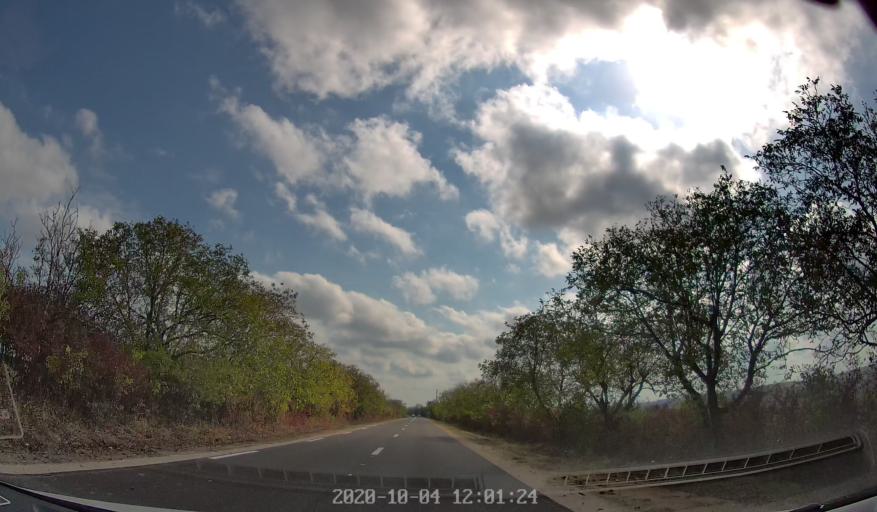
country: MD
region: Rezina
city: Saharna
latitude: 47.6251
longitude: 28.8885
